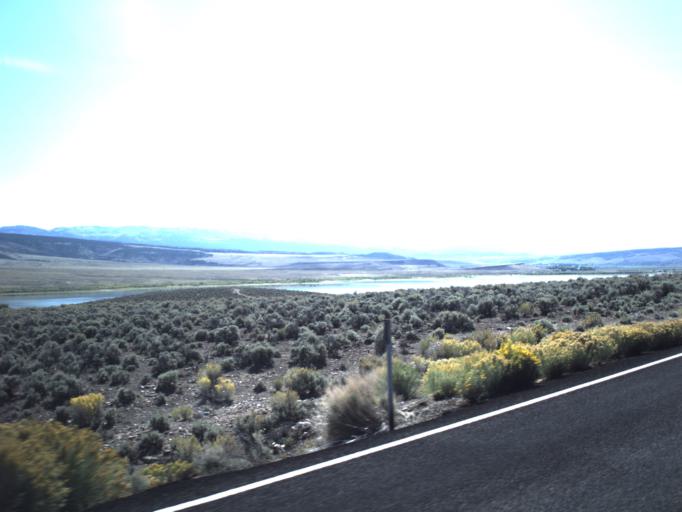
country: US
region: Utah
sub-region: Piute County
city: Junction
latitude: 38.1968
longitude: -112.0097
